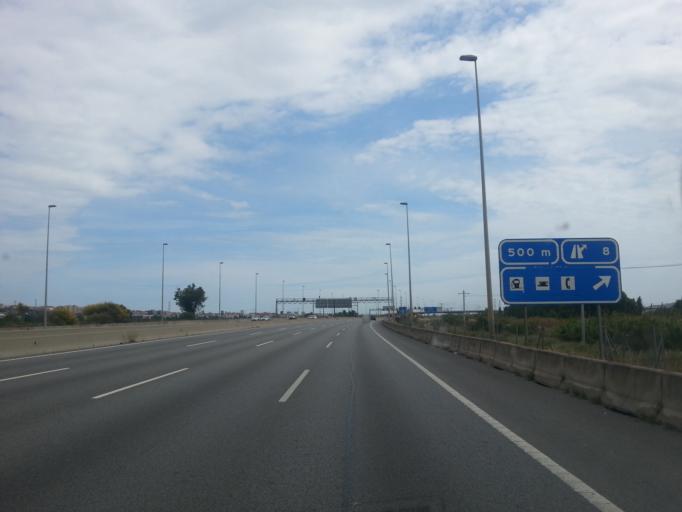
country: ES
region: Catalonia
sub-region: Provincia de Barcelona
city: Sant Vicenc dels Horts
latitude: 41.3997
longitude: 2.0205
